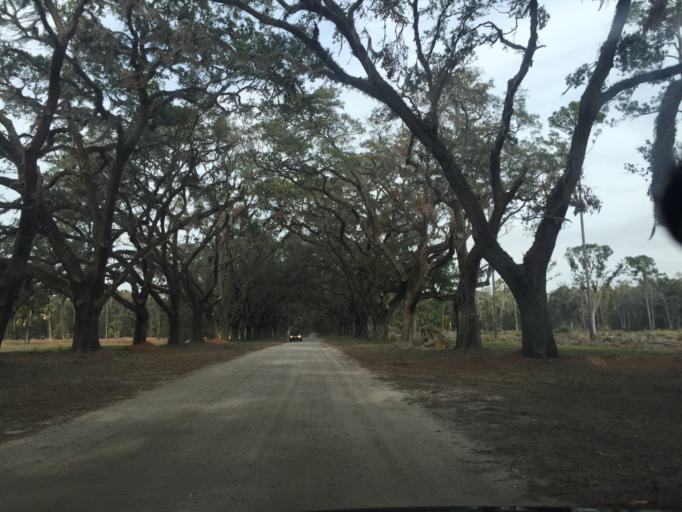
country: US
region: Georgia
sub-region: Chatham County
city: Isle of Hope
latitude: 31.9686
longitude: -81.0692
